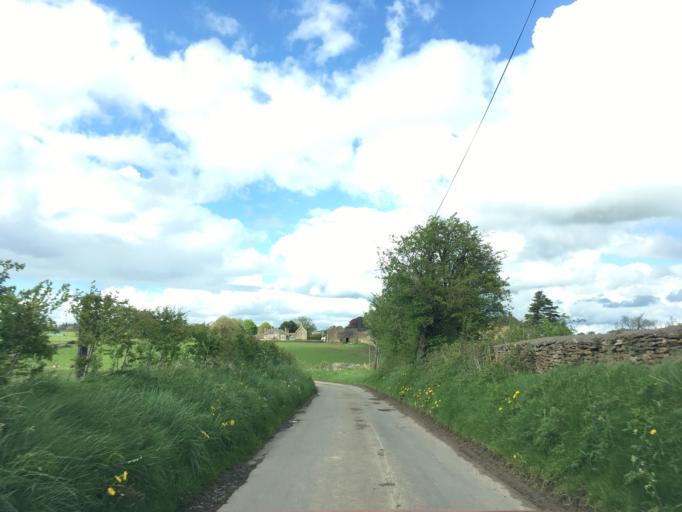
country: GB
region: England
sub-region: Wiltshire
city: Luckington
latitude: 51.5882
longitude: -2.2658
